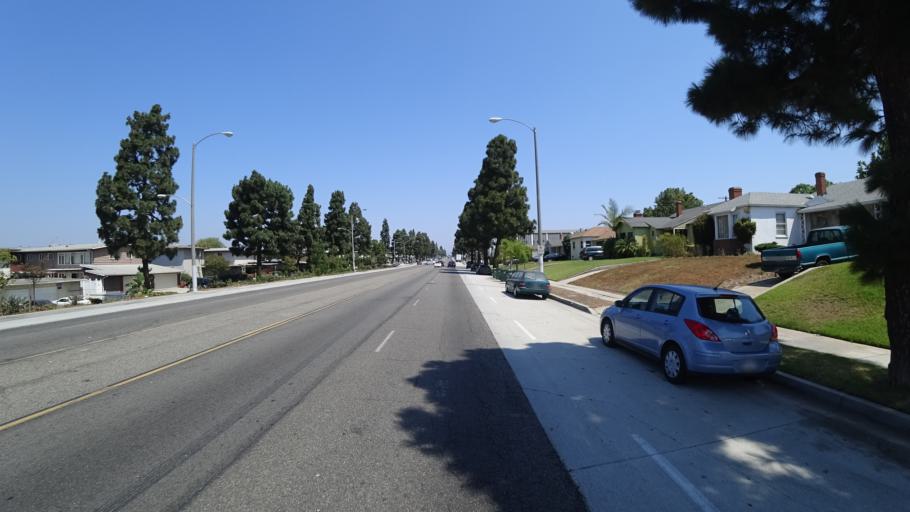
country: US
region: California
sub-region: Los Angeles County
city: Westmont
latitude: 33.9479
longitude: -118.3264
